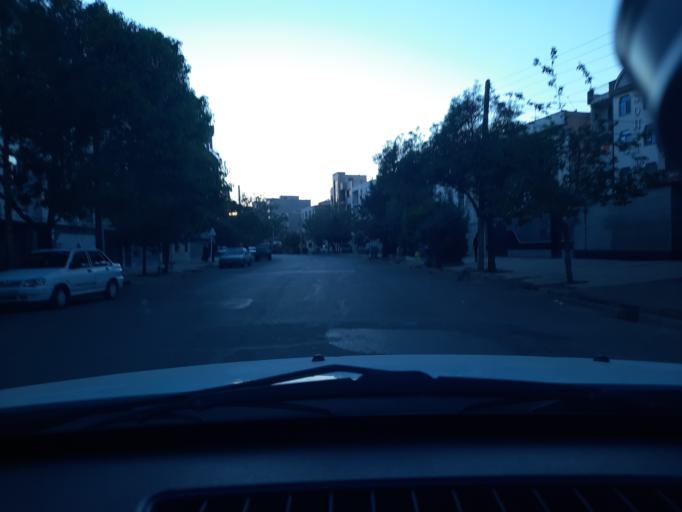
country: IR
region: Qazvin
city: Qazvin
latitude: 36.2989
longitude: 50.0156
